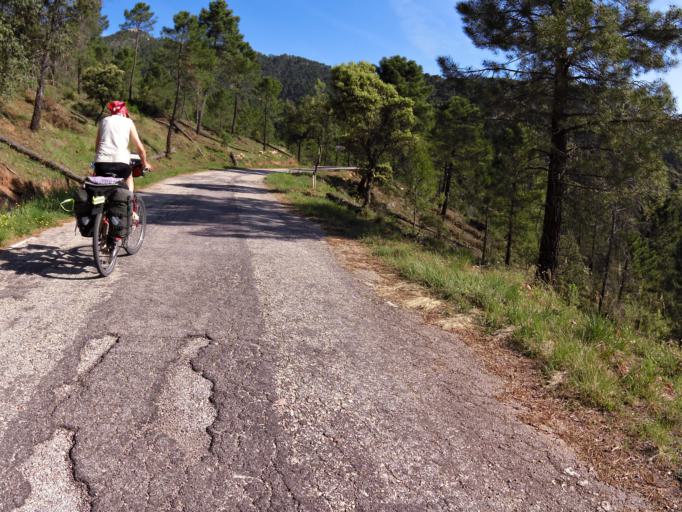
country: ES
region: Castille-La Mancha
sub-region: Provincia de Albacete
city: Riopar
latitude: 38.5199
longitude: -2.4550
